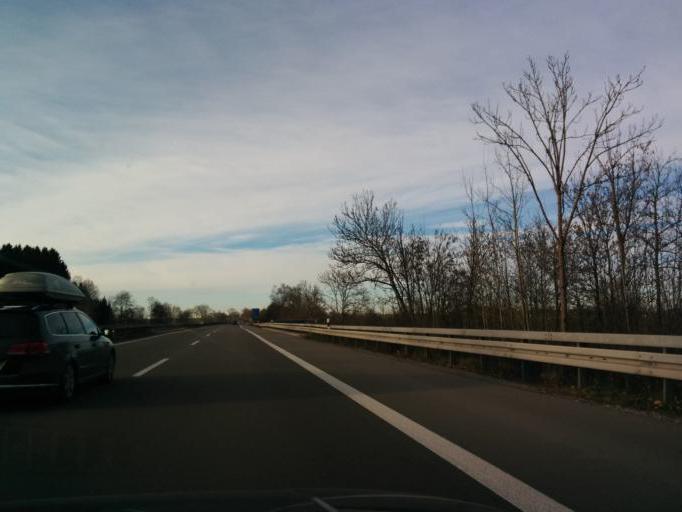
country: DE
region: Bavaria
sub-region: Swabia
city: Betzigau
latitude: 47.7249
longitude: 10.3564
